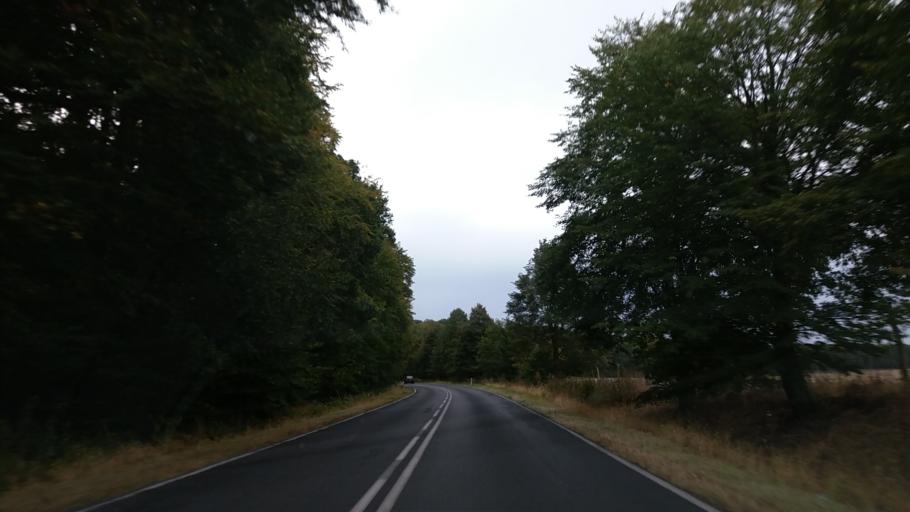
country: PL
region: West Pomeranian Voivodeship
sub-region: Powiat mysliborski
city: Barlinek
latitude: 52.9525
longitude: 15.1839
